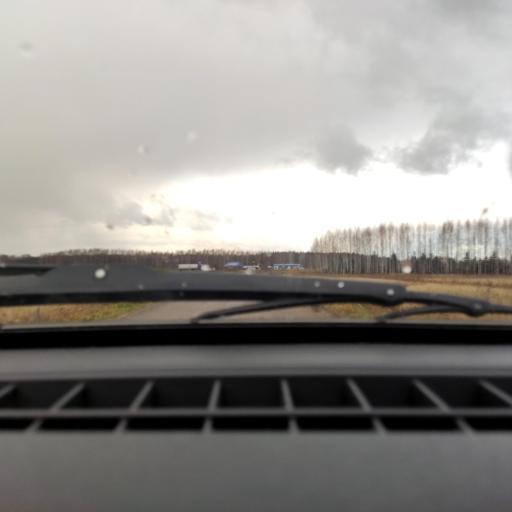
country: RU
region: Bashkortostan
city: Iglino
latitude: 54.7434
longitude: 56.3176
